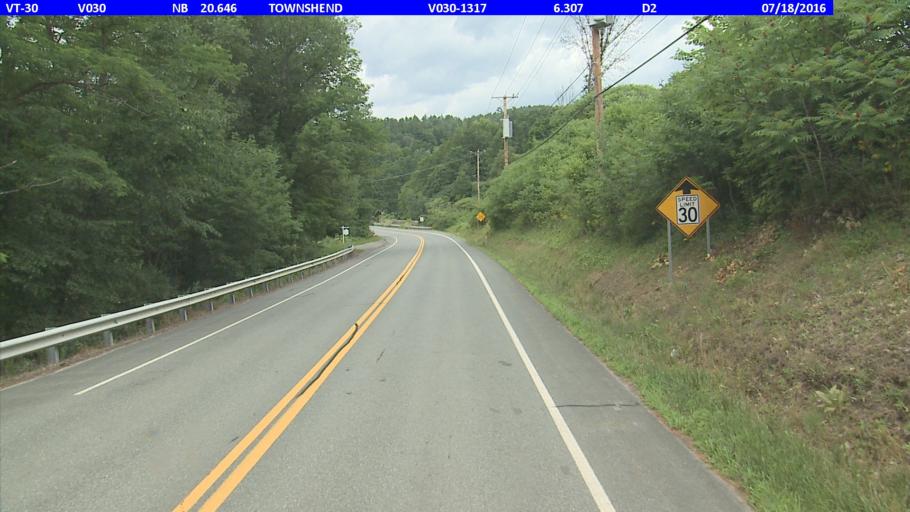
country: US
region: Vermont
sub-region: Windham County
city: Newfane
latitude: 43.0824
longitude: -72.7080
